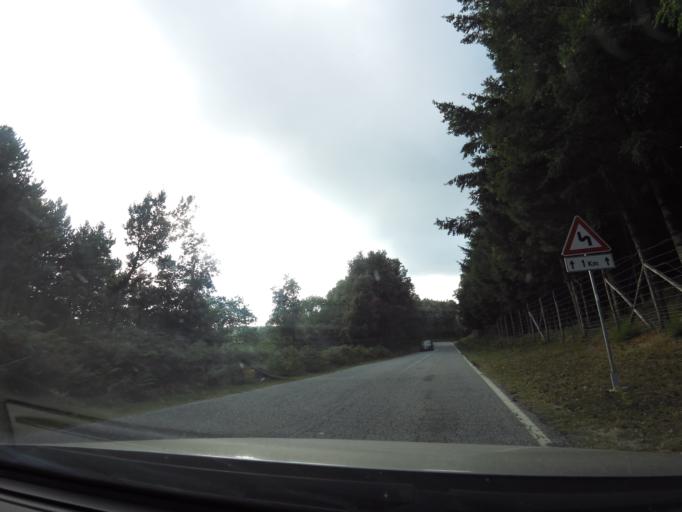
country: IT
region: Calabria
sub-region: Provincia di Vibo-Valentia
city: Nardodipace
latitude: 38.4769
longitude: 16.3943
